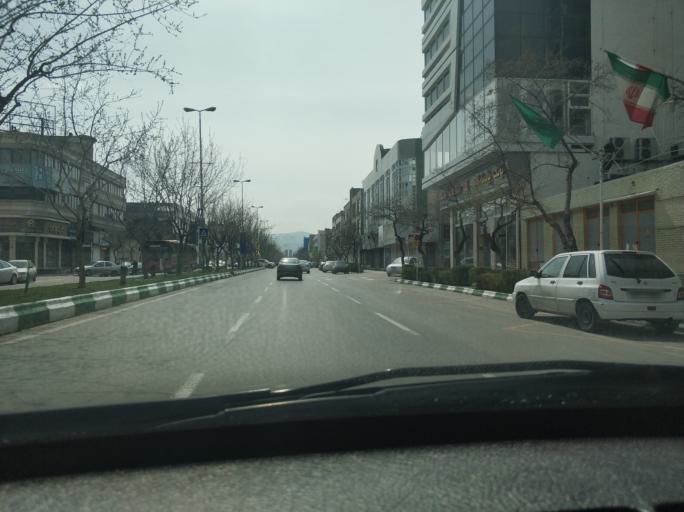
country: IR
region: Razavi Khorasan
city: Mashhad
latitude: 36.3046
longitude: 59.5654
